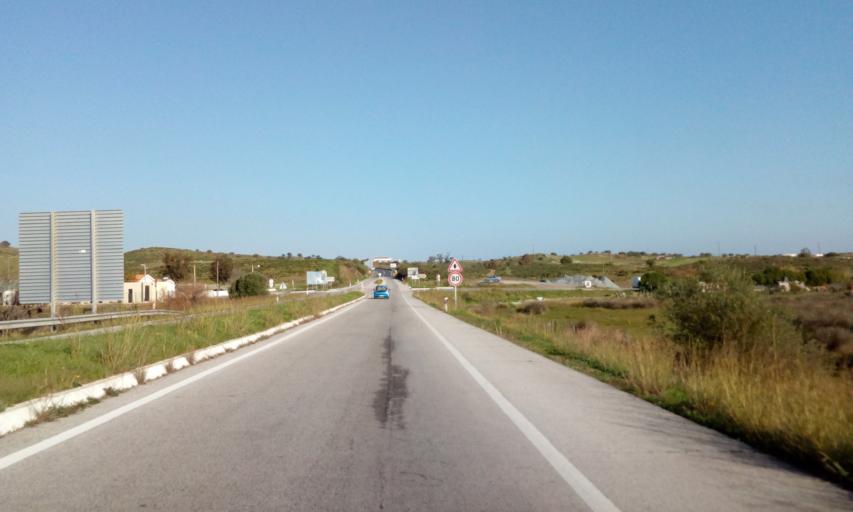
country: PT
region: Faro
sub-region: Castro Marim
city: Castro Marim
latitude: 37.2333
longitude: -7.4477
